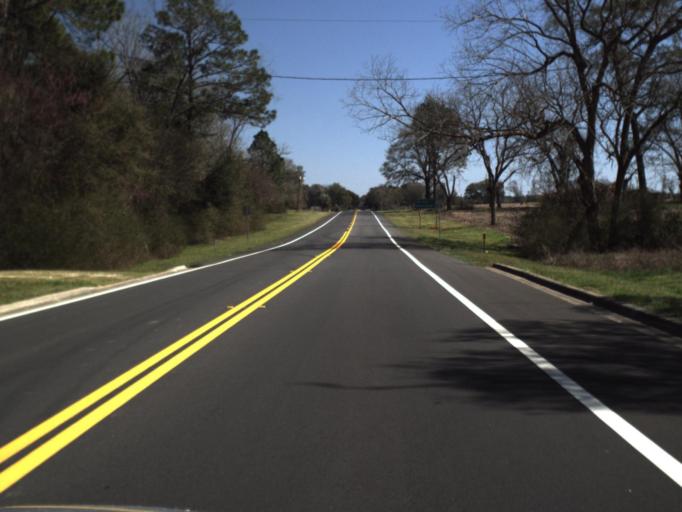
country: US
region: Florida
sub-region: Jackson County
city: Malone
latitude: 30.8700
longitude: -85.1496
